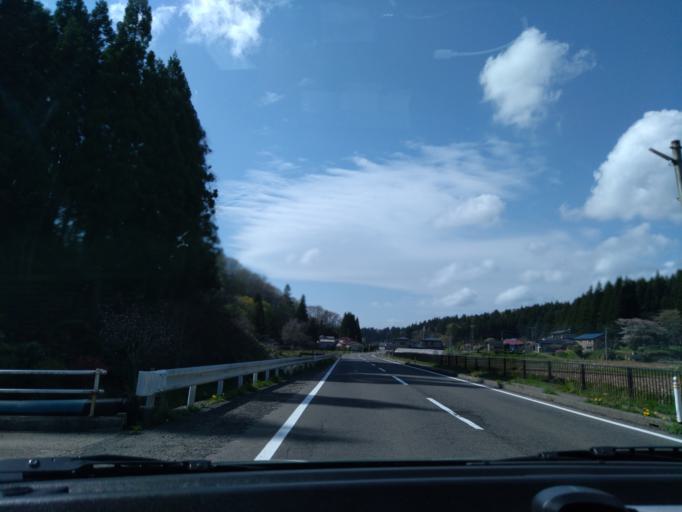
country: JP
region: Akita
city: Akita
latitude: 39.7081
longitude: 140.2065
